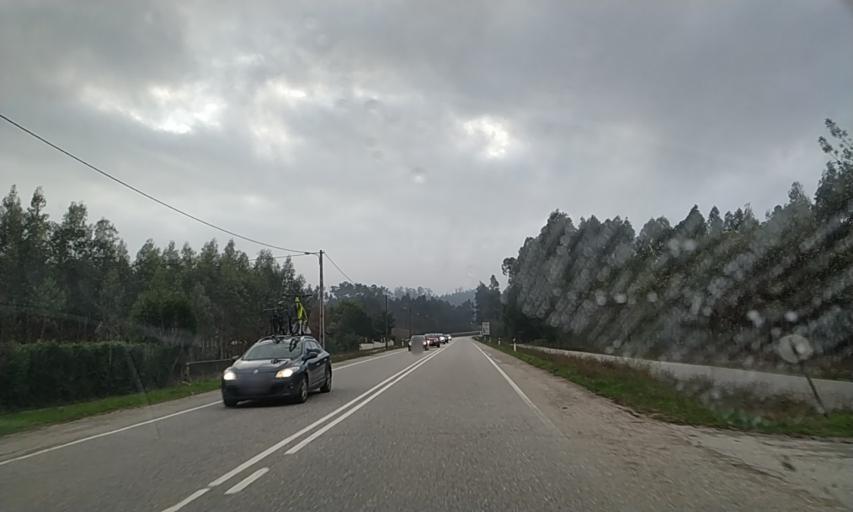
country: PT
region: Viseu
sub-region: Mortagua
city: Mortagua
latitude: 40.3957
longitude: -8.2490
